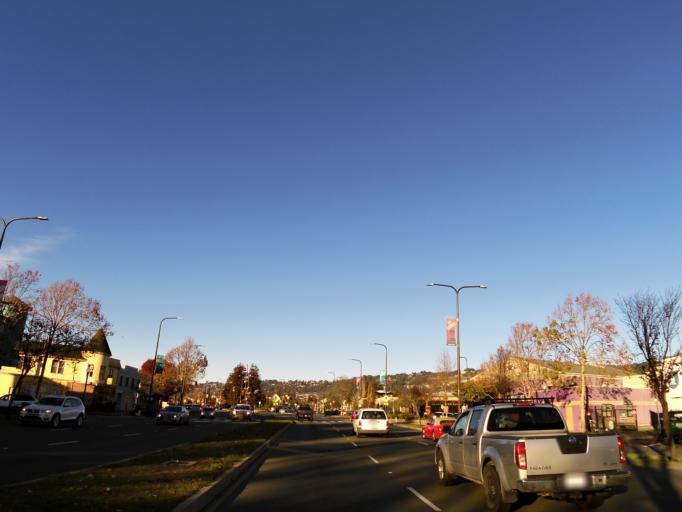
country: US
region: California
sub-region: Alameda County
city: Berkeley
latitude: 37.8501
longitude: -122.2709
